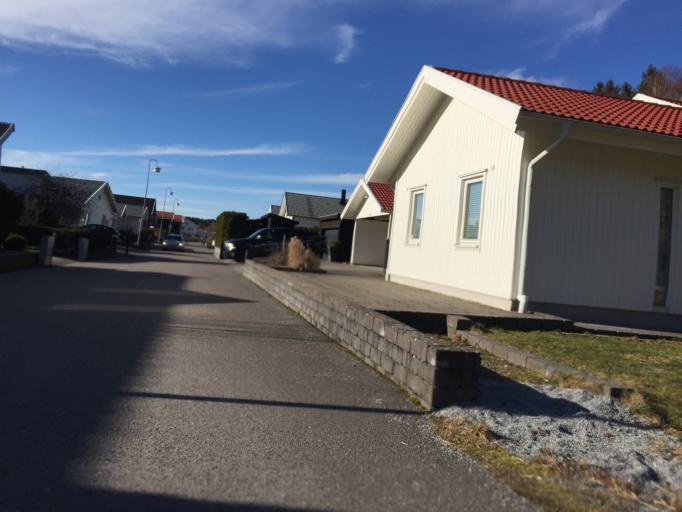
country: SE
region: Vaestra Goetaland
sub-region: Kungalvs Kommun
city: Kungalv
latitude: 57.8955
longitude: 11.9548
